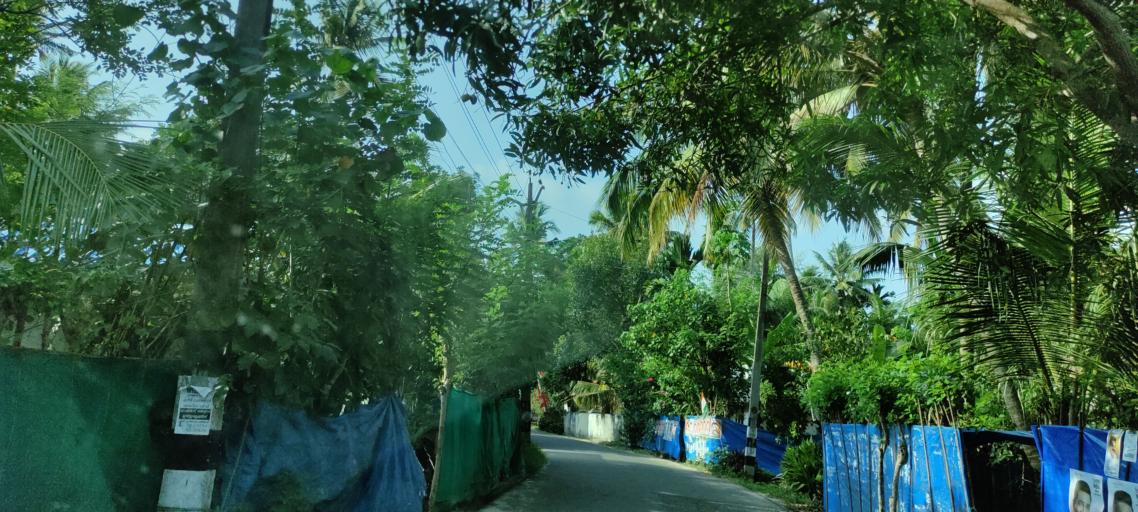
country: IN
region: Kerala
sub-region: Alappuzha
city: Vayalar
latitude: 9.7128
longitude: 76.2880
